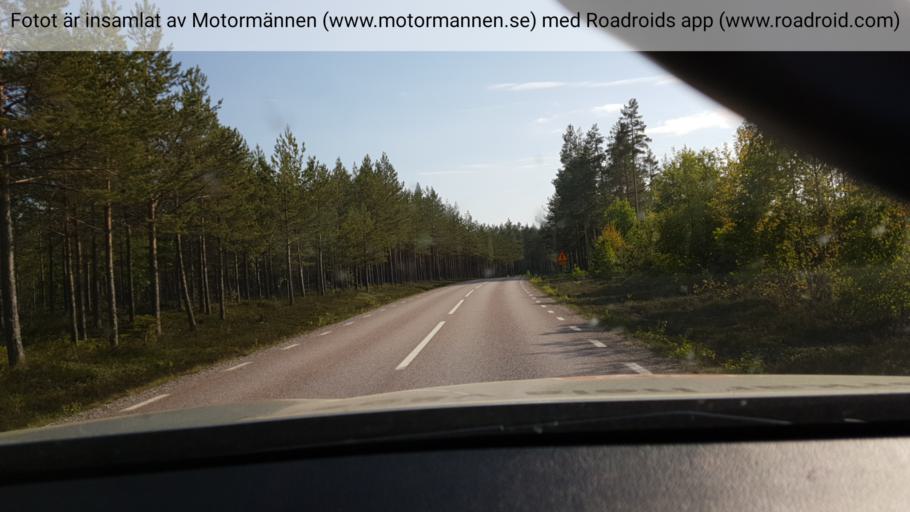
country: SE
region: Gaevleborg
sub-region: Sandvikens Kommun
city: Arsunda
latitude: 60.4710
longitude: 16.7093
